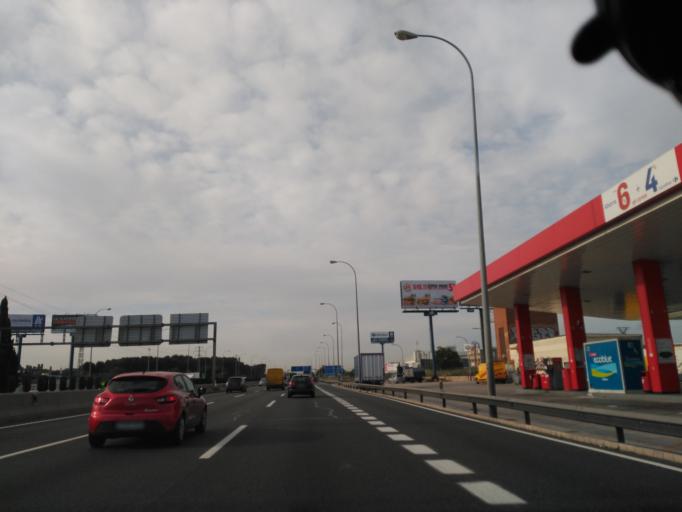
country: ES
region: Madrid
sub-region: Provincia de Madrid
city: Villaverde
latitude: 40.3156
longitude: -3.6922
